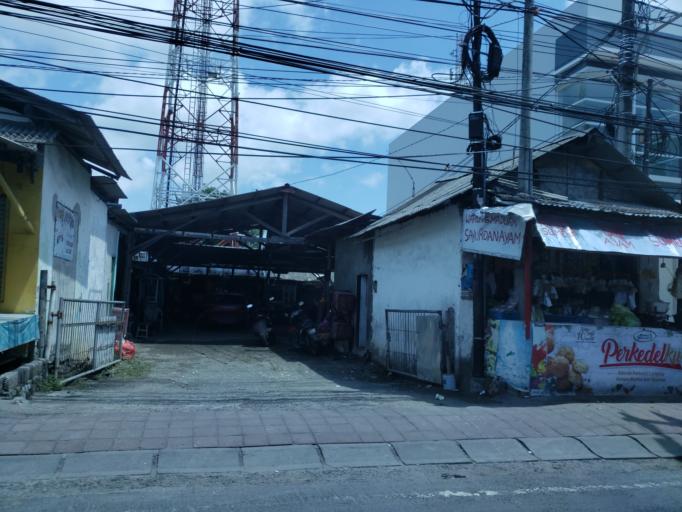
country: ID
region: Bali
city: Jimbaran
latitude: -8.7760
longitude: 115.1711
